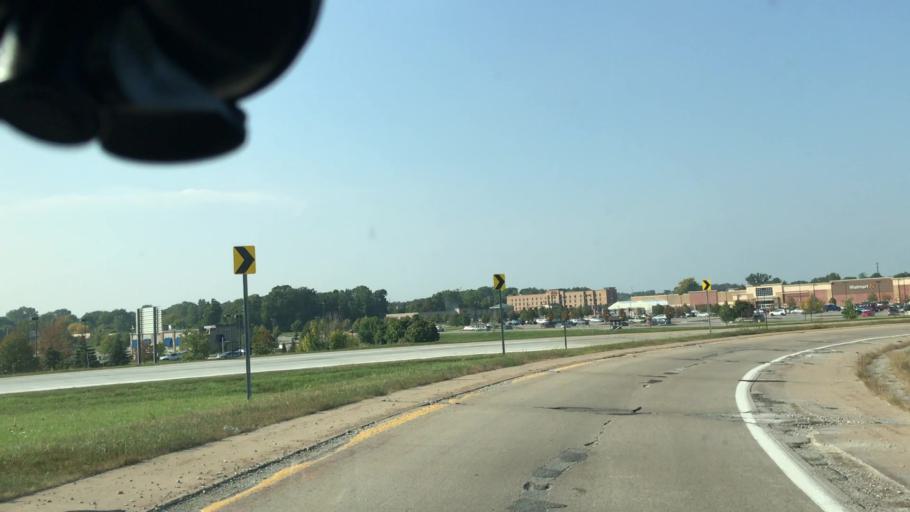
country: US
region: Michigan
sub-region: Macomb County
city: Mount Clemens
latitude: 42.6309
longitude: -82.8514
